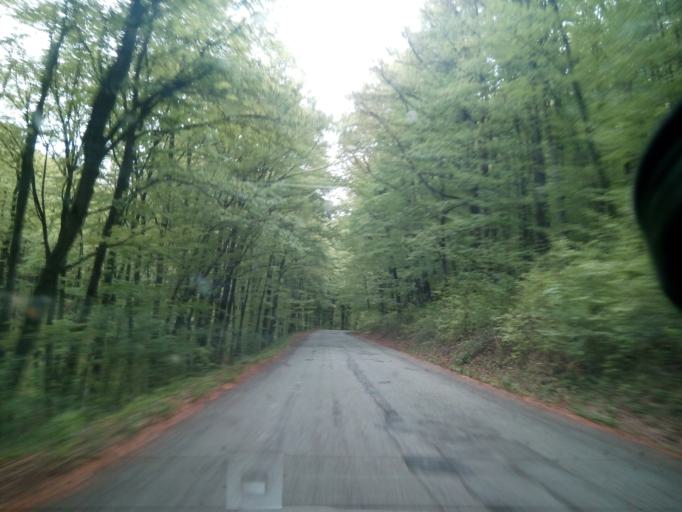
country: SK
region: Kosicky
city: Secovce
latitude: 48.8111
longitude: 21.5163
